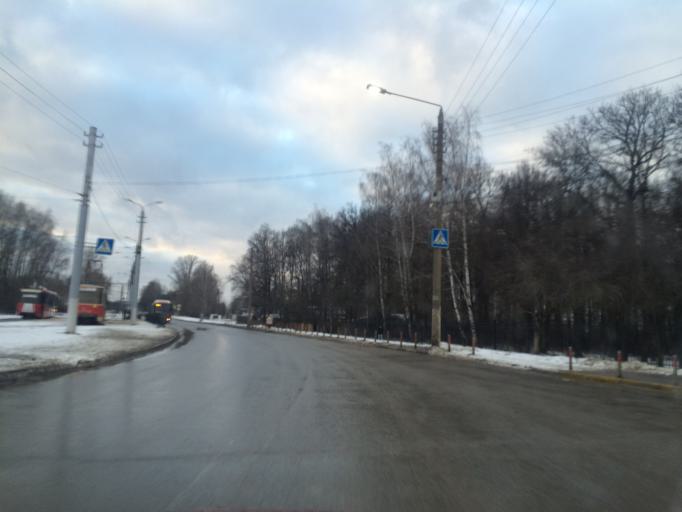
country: RU
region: Tula
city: Tula
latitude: 54.2189
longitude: 37.7066
